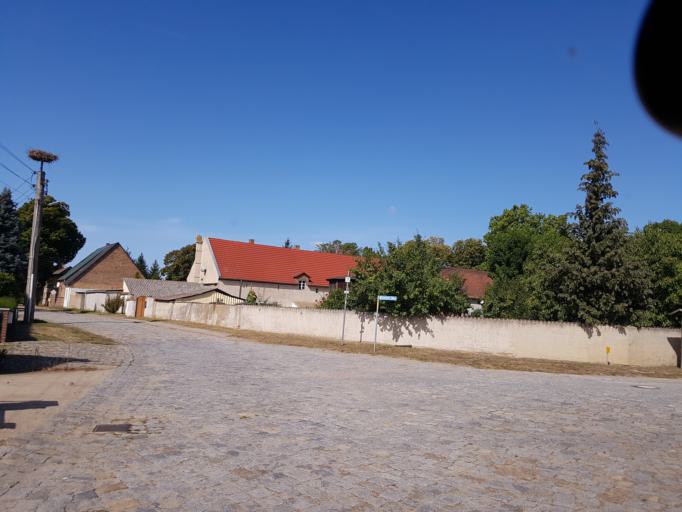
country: DE
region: Brandenburg
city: Drahnsdorf
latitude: 51.8528
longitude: 13.6161
